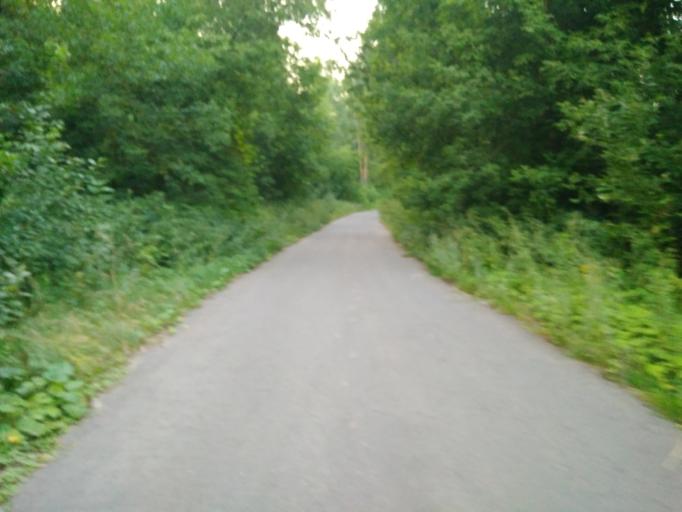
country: RU
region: Moskovskaya
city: Zhukovskiy
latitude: 55.5777
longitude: 38.1174
